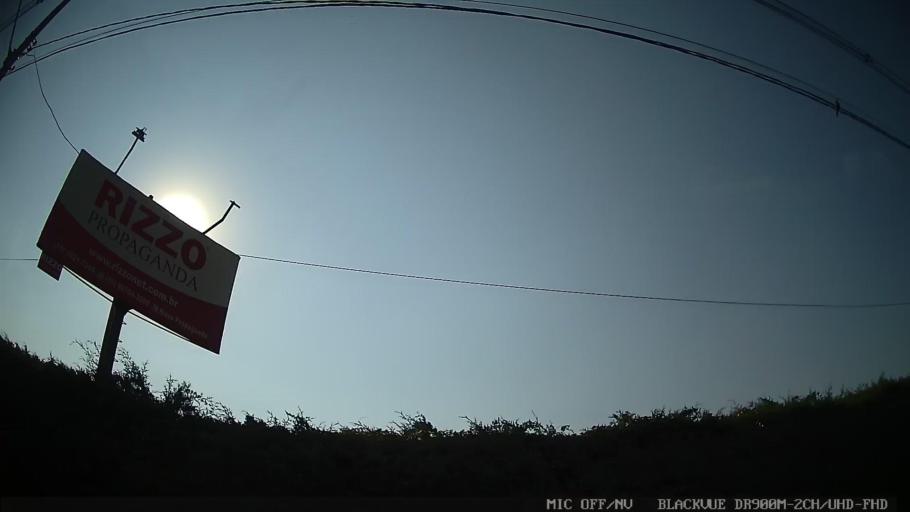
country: BR
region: Sao Paulo
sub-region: Itatiba
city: Itatiba
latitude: -22.9901
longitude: -46.8464
